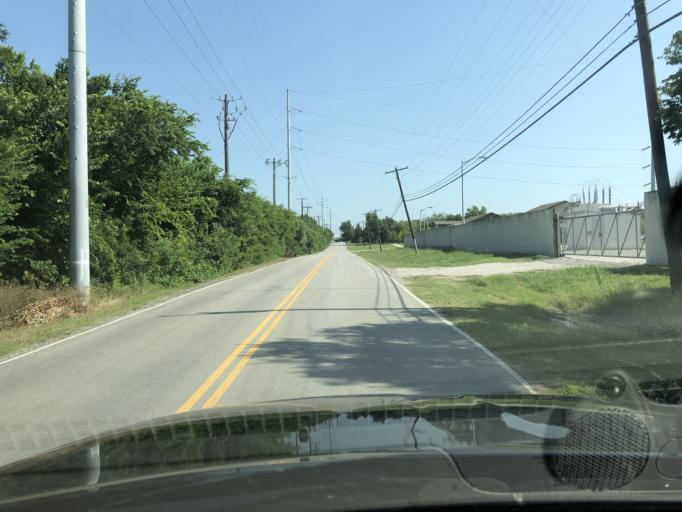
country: US
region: Texas
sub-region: Dallas County
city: Sunnyvale
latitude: 32.8445
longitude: -96.5696
